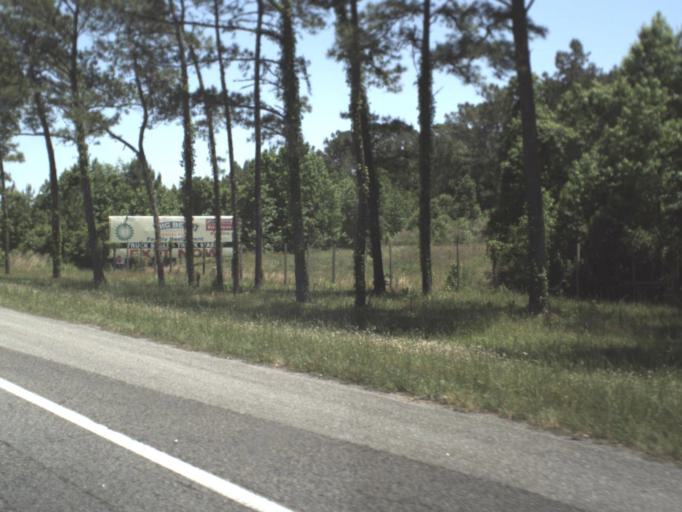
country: US
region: Florida
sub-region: Jefferson County
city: Monticello
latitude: 30.4862
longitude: -84.0309
